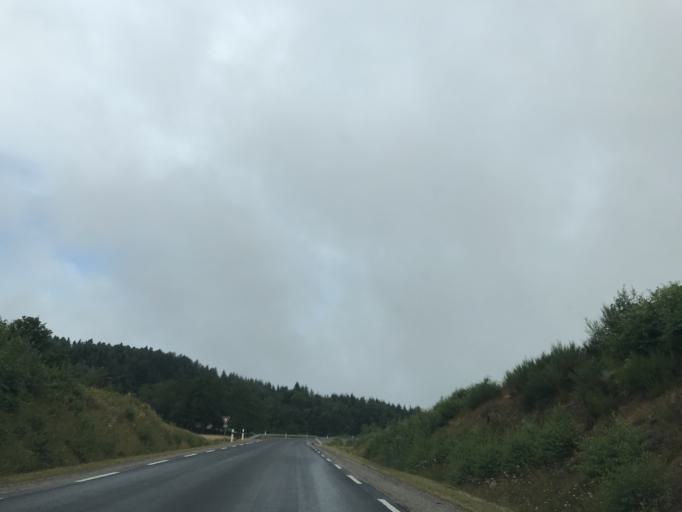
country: FR
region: Auvergne
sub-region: Departement de la Haute-Loire
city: Fontannes
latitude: 45.3497
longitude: 3.7356
